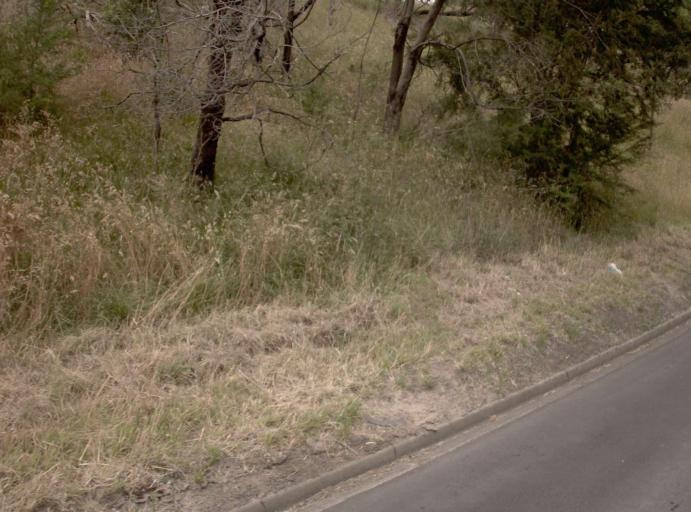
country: AU
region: Victoria
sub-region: Latrobe
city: Traralgon
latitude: -38.2469
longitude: 146.5245
